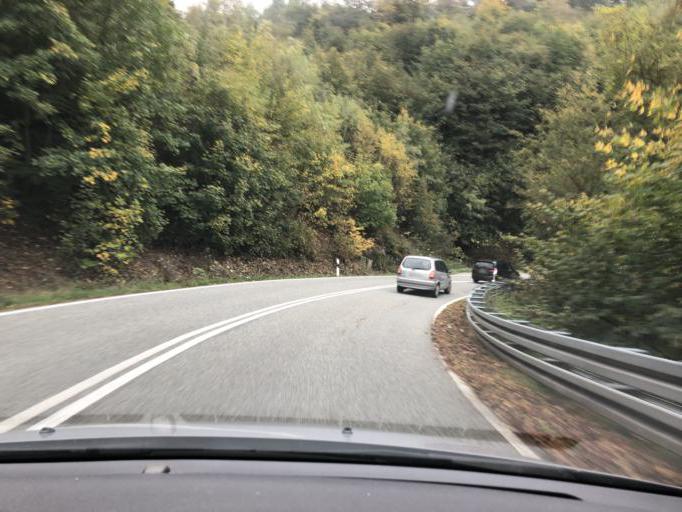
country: DE
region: Saxony-Anhalt
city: Kelbra
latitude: 51.4163
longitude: 11.0716
